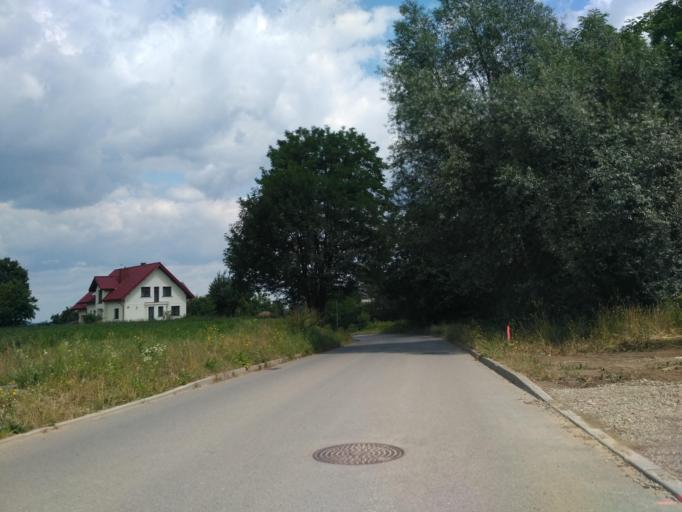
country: PL
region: Subcarpathian Voivodeship
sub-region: Powiat debicki
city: Pilzno
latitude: 49.9690
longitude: 21.2912
